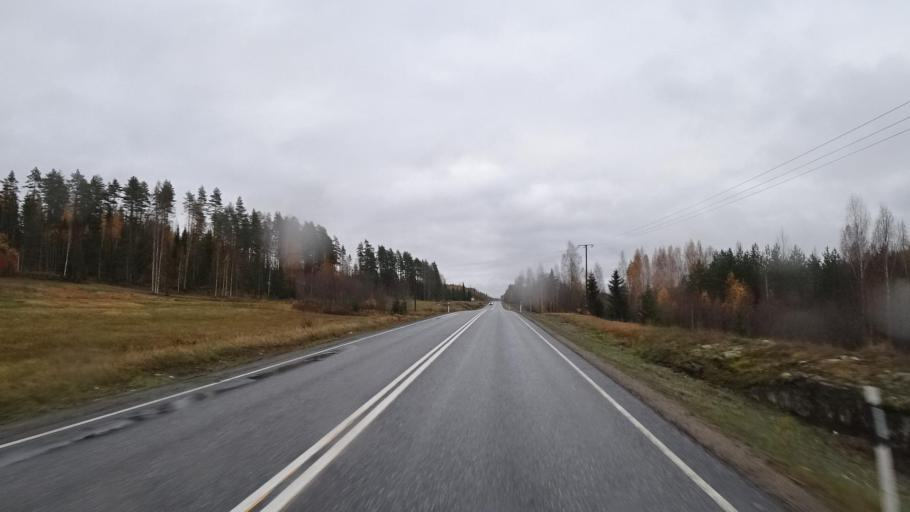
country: FI
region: Southern Savonia
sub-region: Savonlinna
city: Heinaevesi
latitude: 62.5258
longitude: 28.5618
